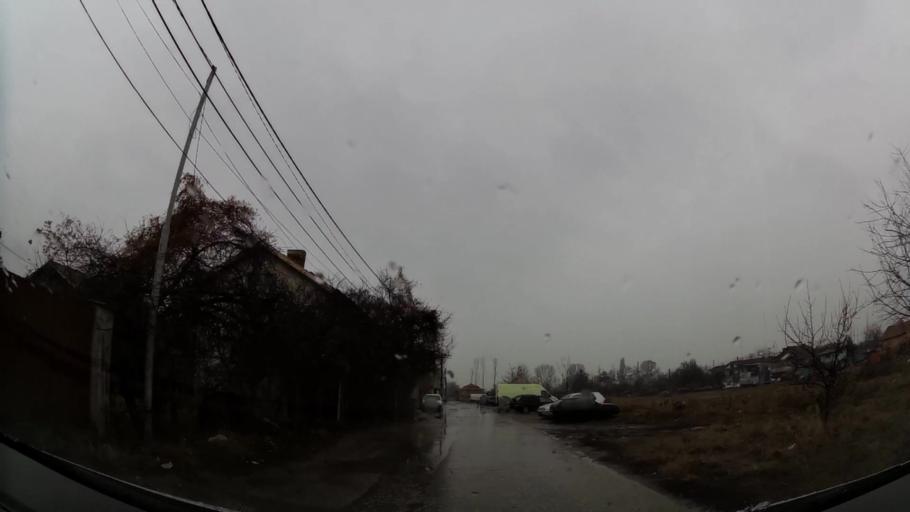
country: BG
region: Sofia-Capital
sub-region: Stolichna Obshtina
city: Sofia
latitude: 42.6604
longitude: 23.4256
